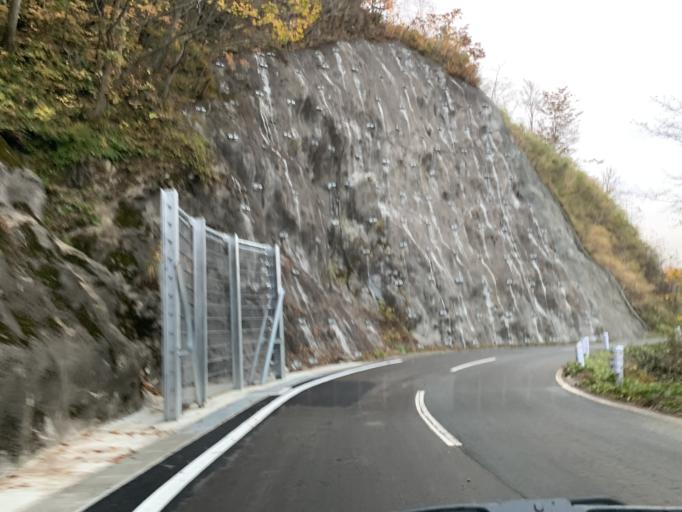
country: JP
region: Iwate
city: Mizusawa
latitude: 39.1108
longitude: 140.8506
